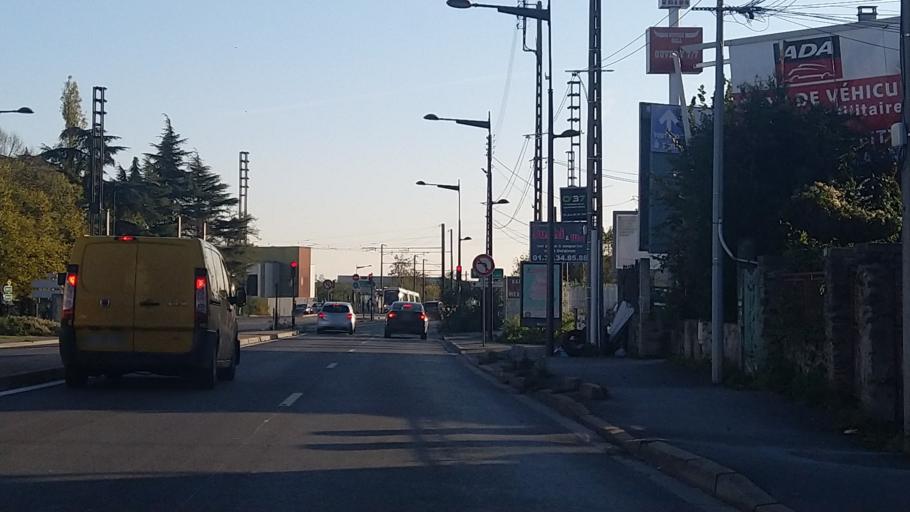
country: FR
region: Ile-de-France
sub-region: Departement de Seine-Saint-Denis
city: Pierrefitte-sur-Seine
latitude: 48.9754
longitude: 2.3654
